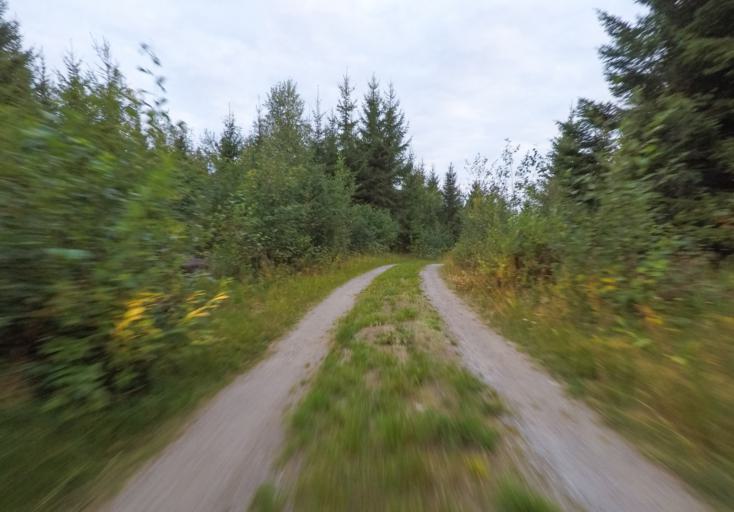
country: FI
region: Central Finland
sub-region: Jyvaeskylae
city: Hankasalmi
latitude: 62.4242
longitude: 26.6639
